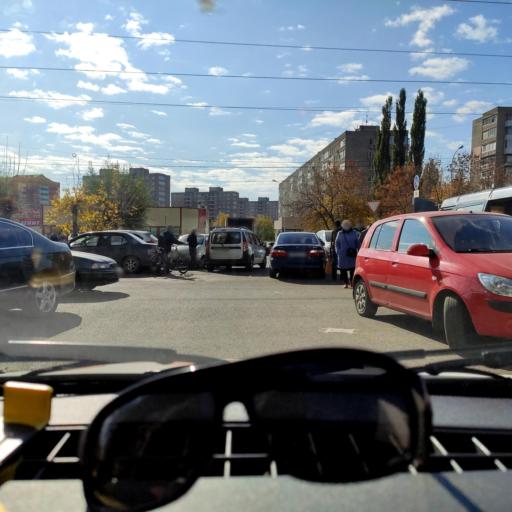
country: RU
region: Bashkortostan
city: Ufa
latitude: 54.7031
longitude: 56.0024
